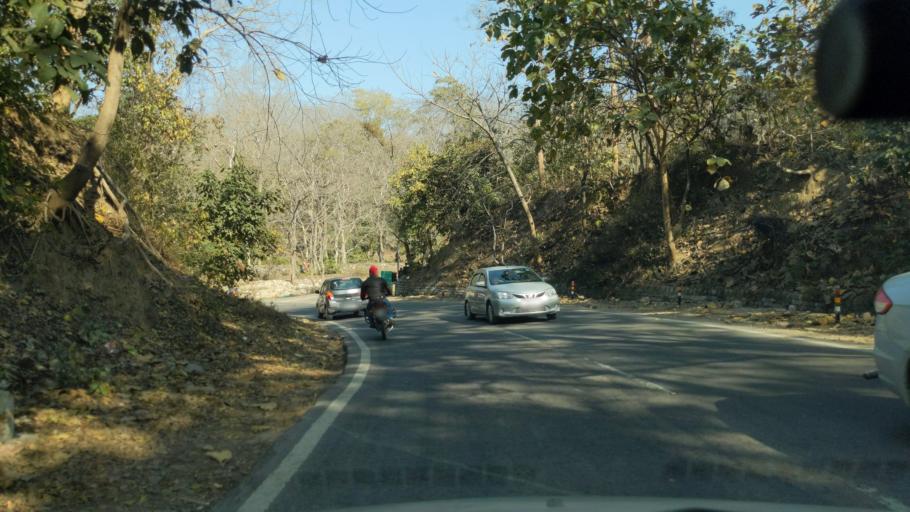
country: IN
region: Uttarakhand
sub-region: Naini Tal
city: Ramnagar
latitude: 29.3851
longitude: 79.1426
